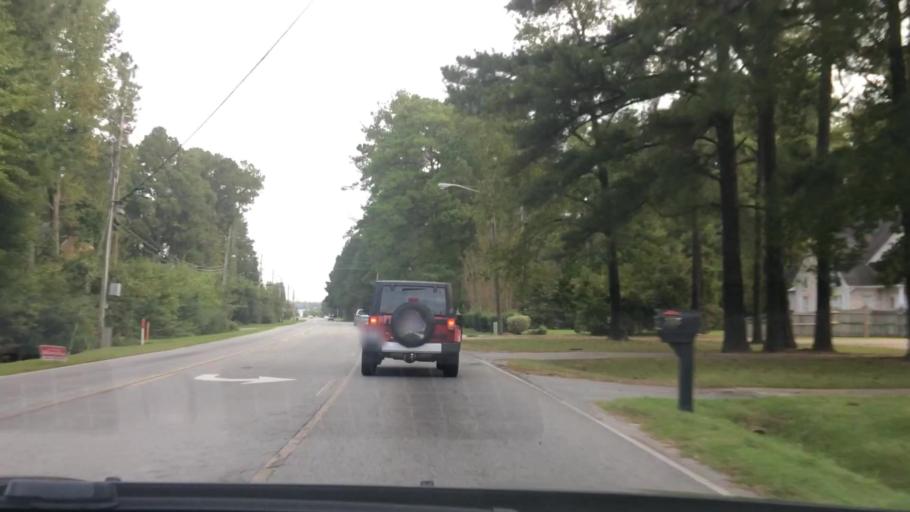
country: US
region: North Carolina
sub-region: Pitt County
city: Summerfield
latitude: 35.5680
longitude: -77.3829
